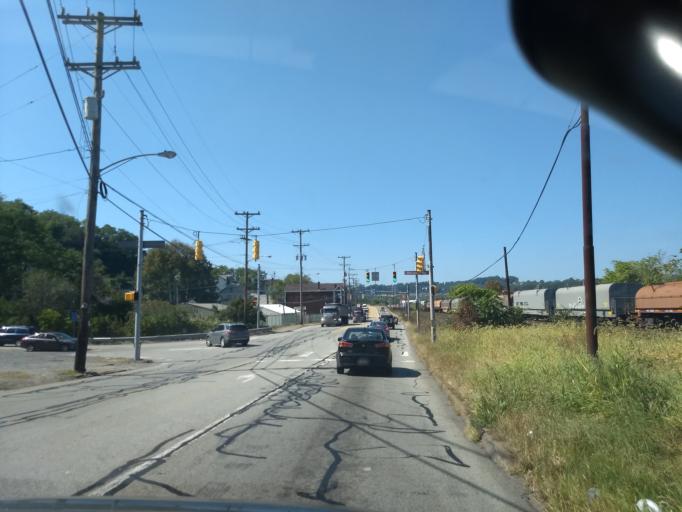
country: US
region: Pennsylvania
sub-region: Allegheny County
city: Whitaker
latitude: 40.4082
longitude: -79.8938
